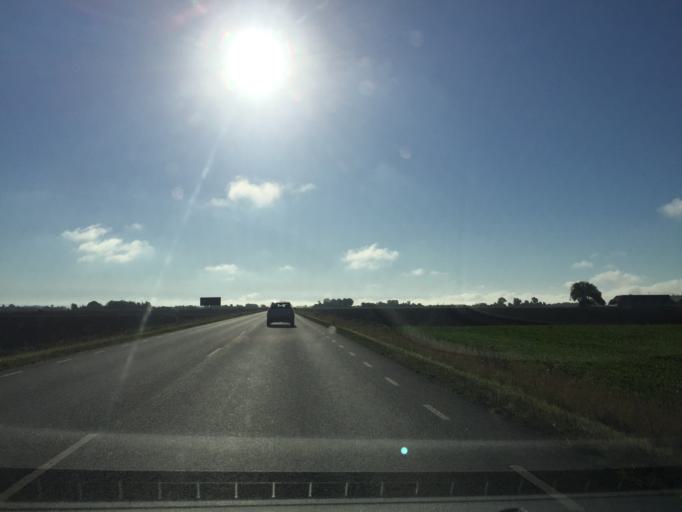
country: SE
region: Skane
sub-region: Lunds Kommun
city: Lund
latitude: 55.6753
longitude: 13.1863
